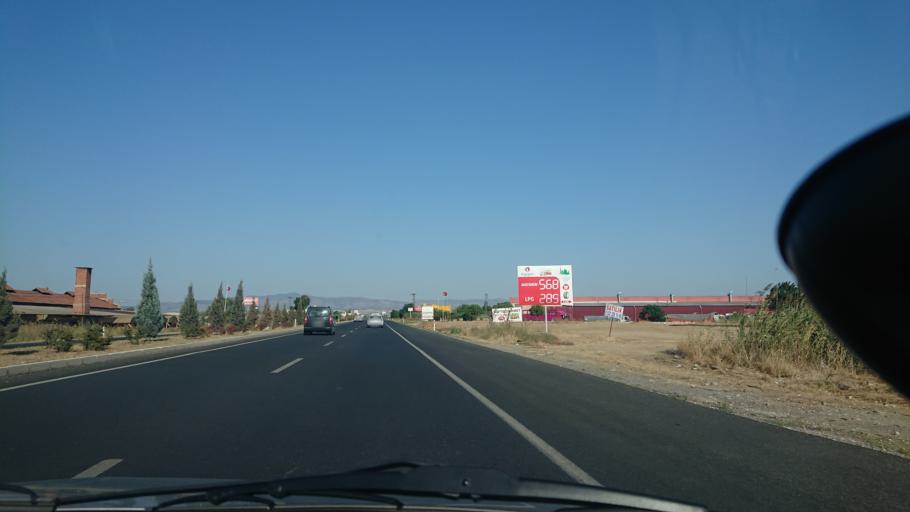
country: TR
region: Manisa
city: Salihli
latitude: 38.5017
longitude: 28.2115
